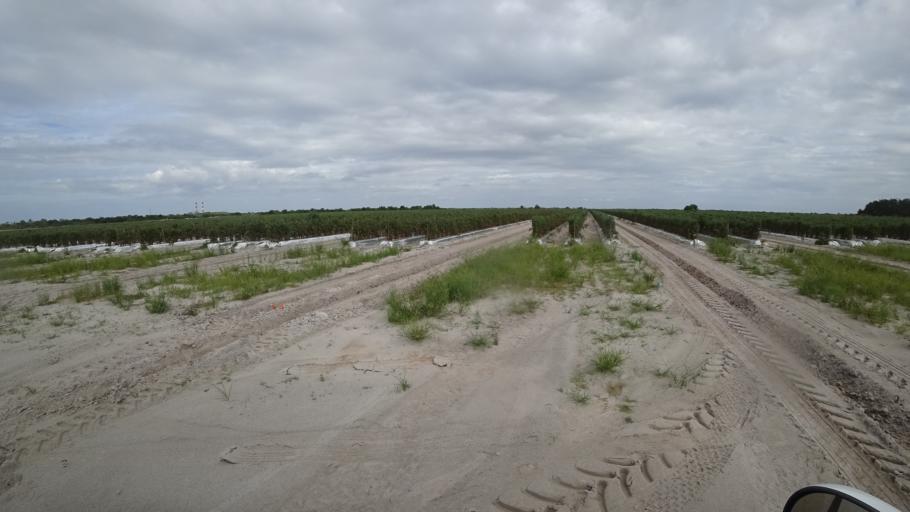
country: US
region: Florida
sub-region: Hillsborough County
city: Wimauma
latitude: 27.5790
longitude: -82.3173
